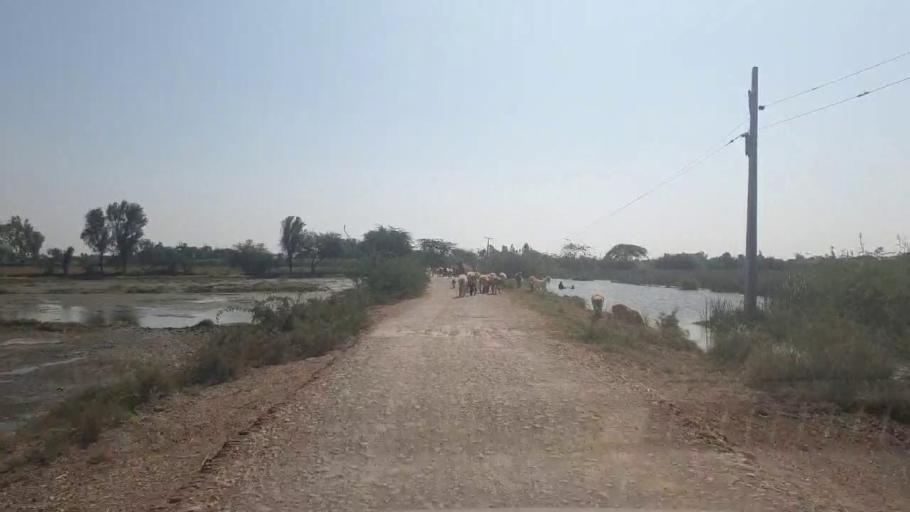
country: PK
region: Sindh
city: Badin
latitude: 24.6347
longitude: 68.9122
